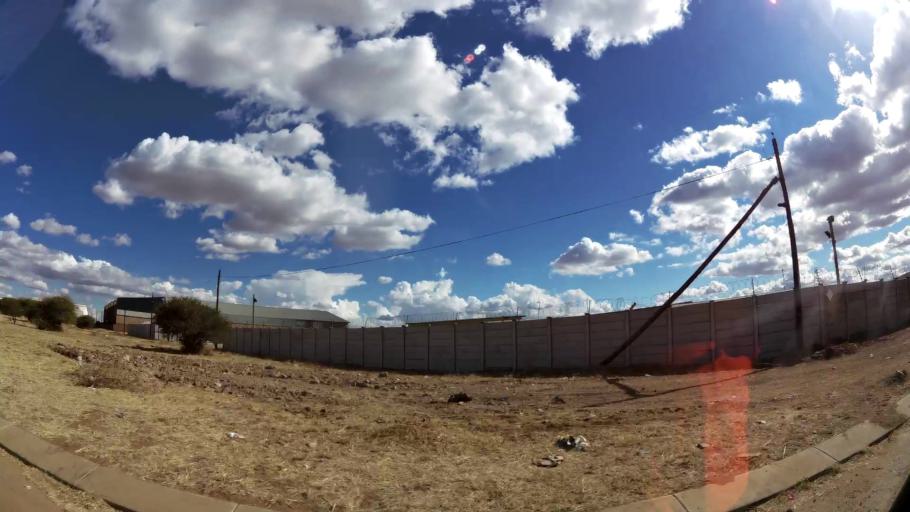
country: ZA
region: Limpopo
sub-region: Capricorn District Municipality
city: Polokwane
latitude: -23.8659
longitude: 29.4824
